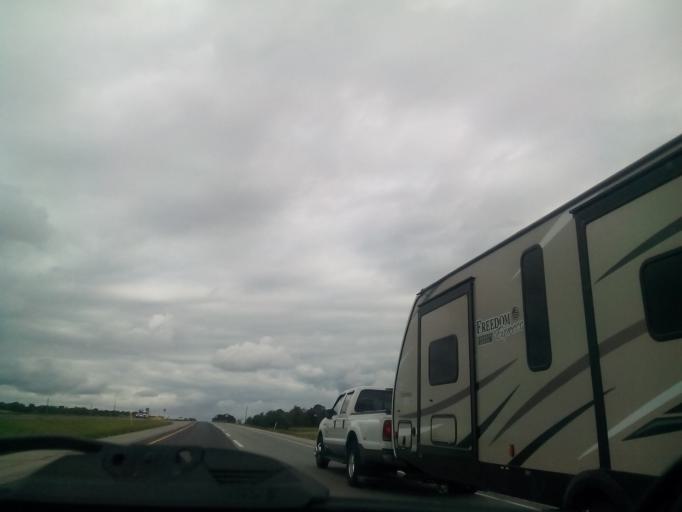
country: US
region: Michigan
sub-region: Saint Joseph County
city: Sturgis
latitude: 41.7403
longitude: -85.2988
